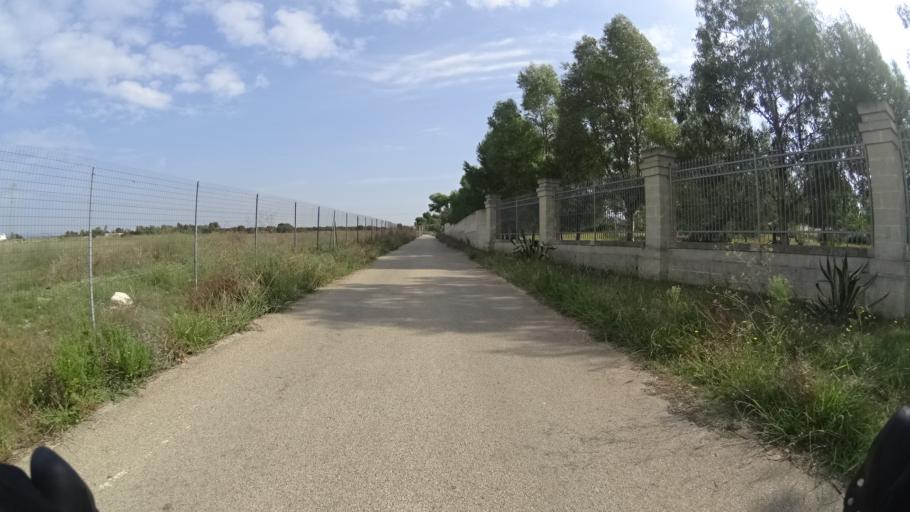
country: IT
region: Apulia
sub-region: Provincia di Taranto
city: San Marzano di San Giuseppe
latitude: 40.4685
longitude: 17.4846
